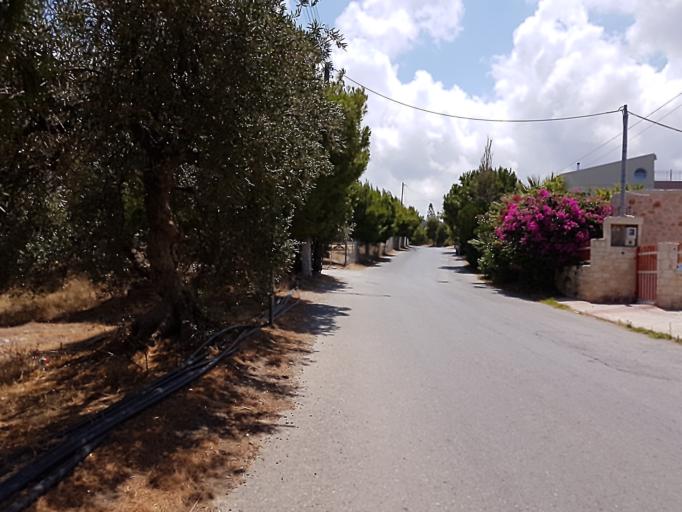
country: GR
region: Crete
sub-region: Nomos Irakleiou
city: Limin Khersonisou
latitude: 35.3107
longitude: 25.3758
